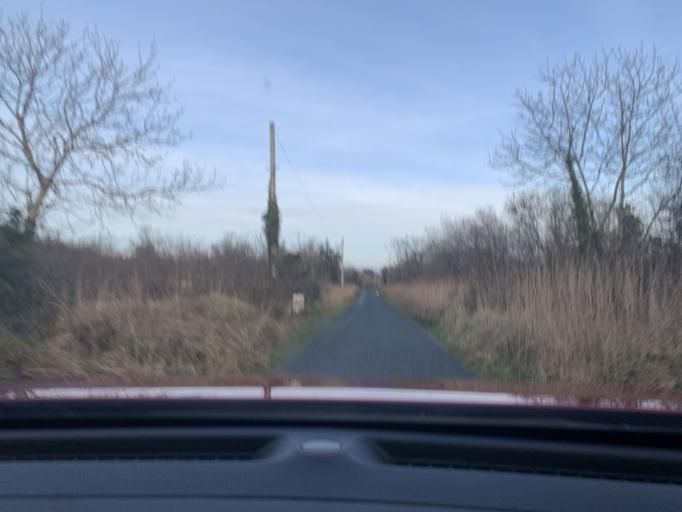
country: IE
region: Connaught
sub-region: Sligo
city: Strandhill
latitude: 54.1780
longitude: -8.6203
